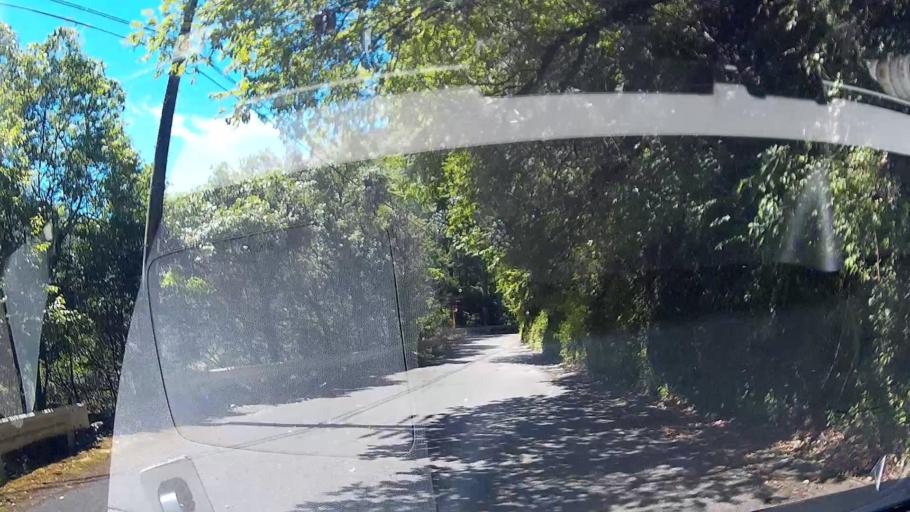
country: JP
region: Shizuoka
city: Shizuoka-shi
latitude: 35.1790
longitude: 138.2832
